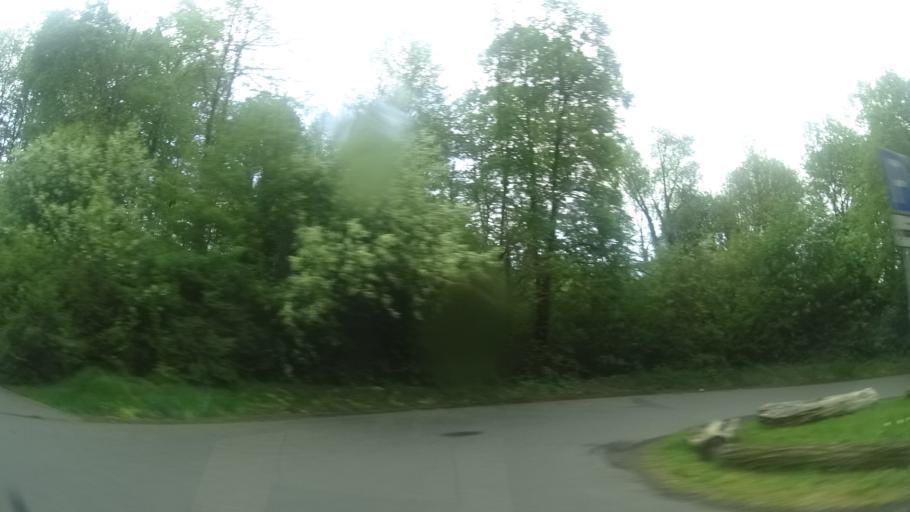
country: DE
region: Hesse
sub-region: Regierungsbezirk Giessen
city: Wetzlar
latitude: 50.5650
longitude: 8.5187
